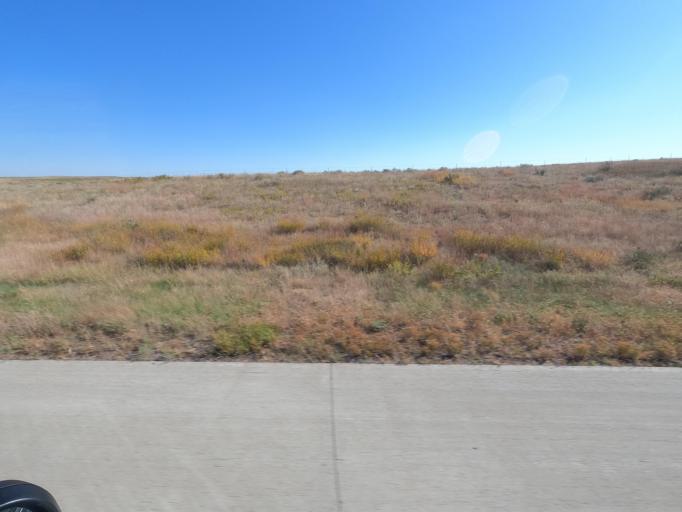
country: US
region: Nebraska
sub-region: Deuel County
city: Chappell
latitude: 40.9166
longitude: -102.4725
